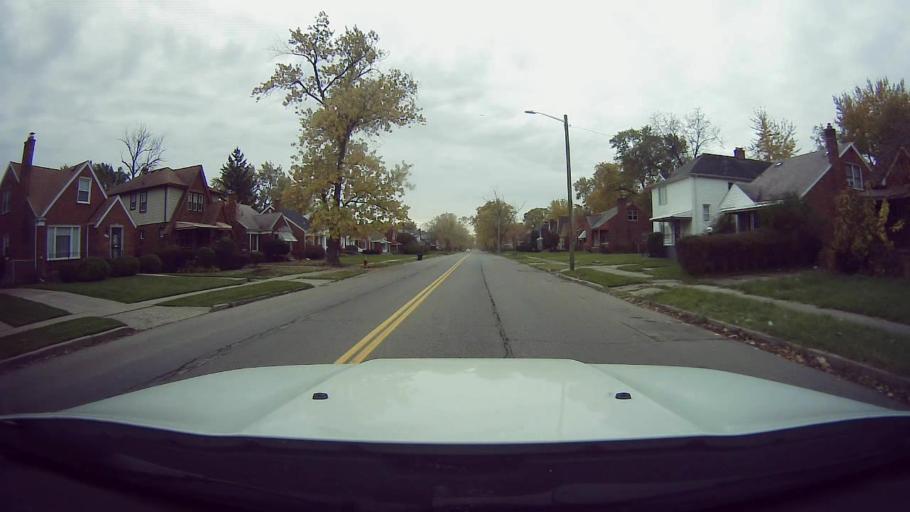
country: US
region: Michigan
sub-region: Oakland County
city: Oak Park
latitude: 42.3986
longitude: -83.1888
